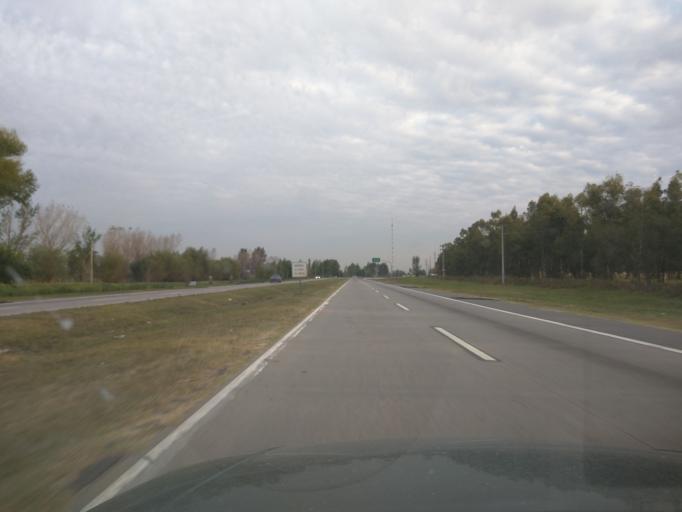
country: AR
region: Buenos Aires
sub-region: Partido de Campana
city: Campana
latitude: -34.2243
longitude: -58.9589
